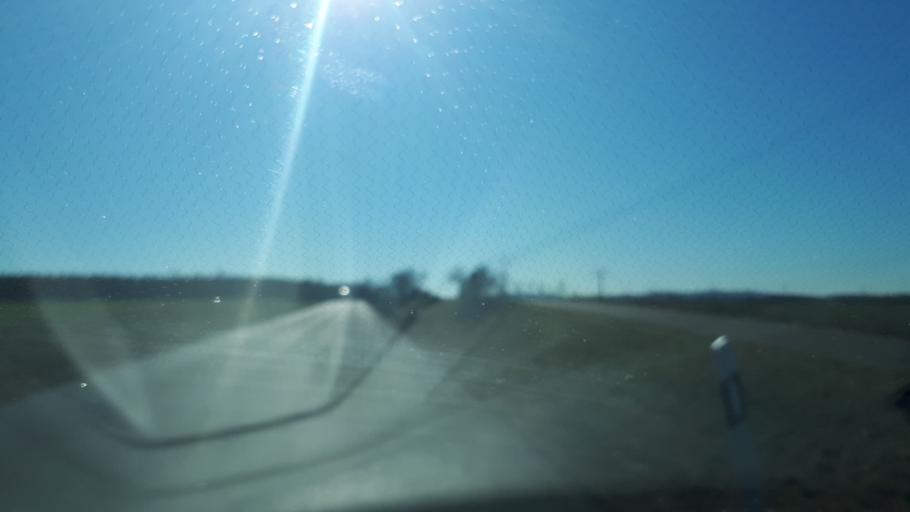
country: DE
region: Rheinland-Pfalz
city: Strotzbusch
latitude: 50.0956
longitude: 6.9645
